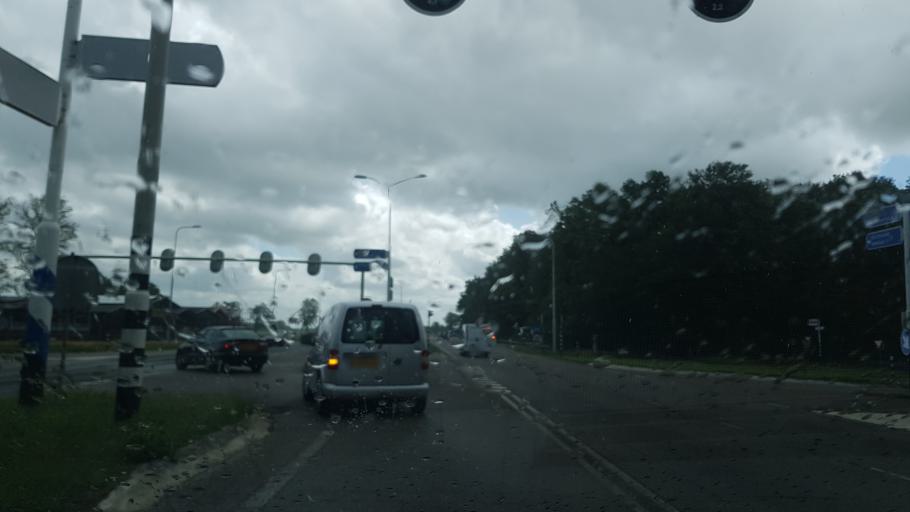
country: NL
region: Friesland
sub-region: Gemeente Tytsjerksteradiel
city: Tytsjerk
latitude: 53.2180
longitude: 5.9082
